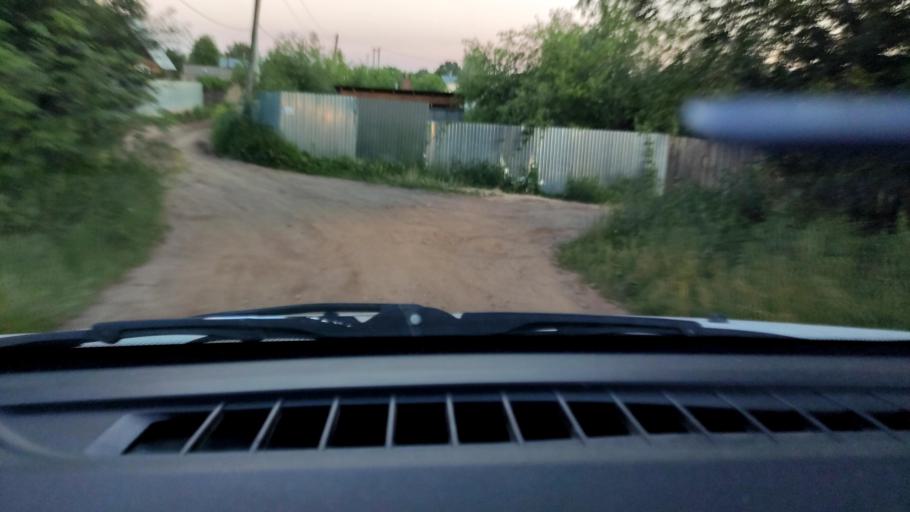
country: RU
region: Perm
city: Kondratovo
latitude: 57.9545
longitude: 56.1458
